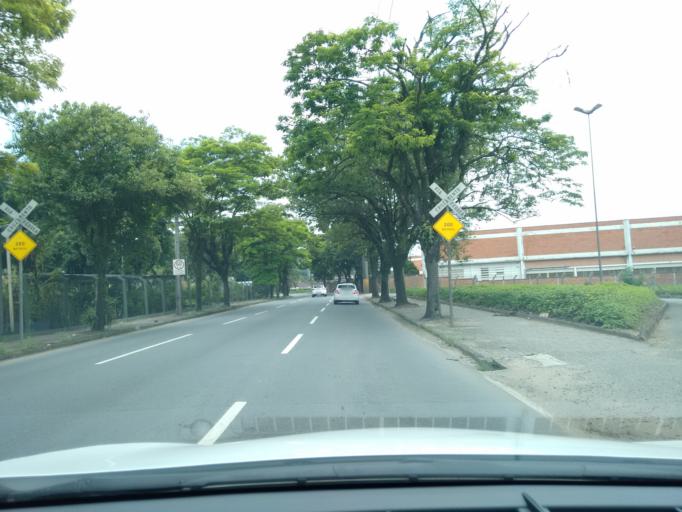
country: BR
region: Santa Catarina
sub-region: Jaragua Do Sul
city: Jaragua do Sul
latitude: -26.4798
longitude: -49.0559
